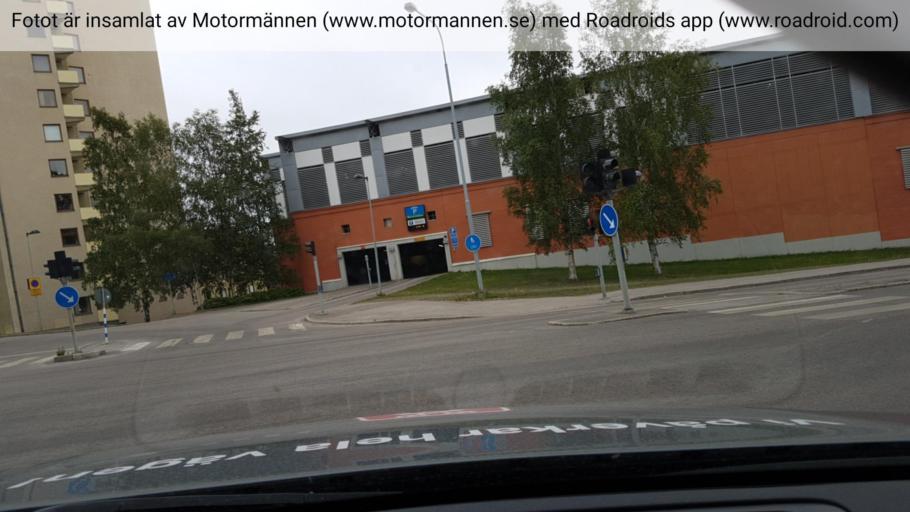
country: SE
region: Vaesternorrland
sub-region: Sundsvalls Kommun
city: Sundsvall
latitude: 62.3950
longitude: 17.3033
